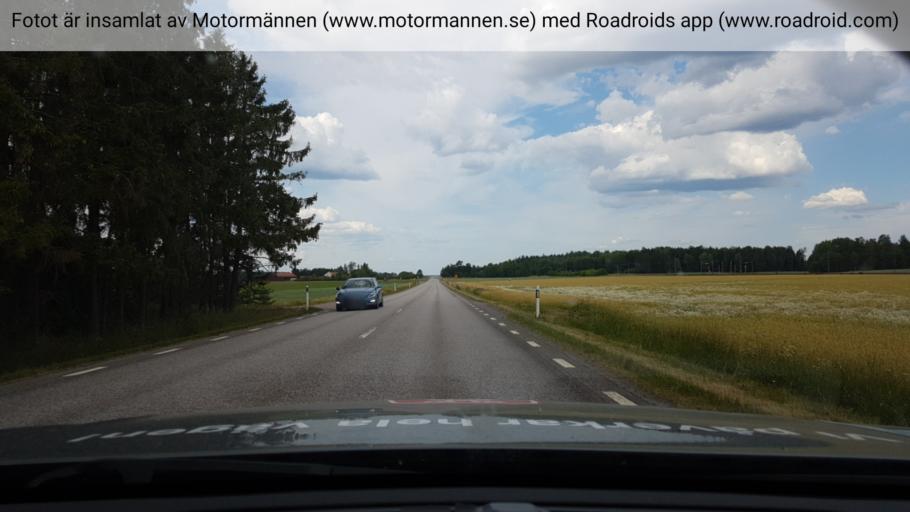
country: SE
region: Vaestmanland
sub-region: Sala Kommun
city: Sala
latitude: 59.8659
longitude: 16.6295
